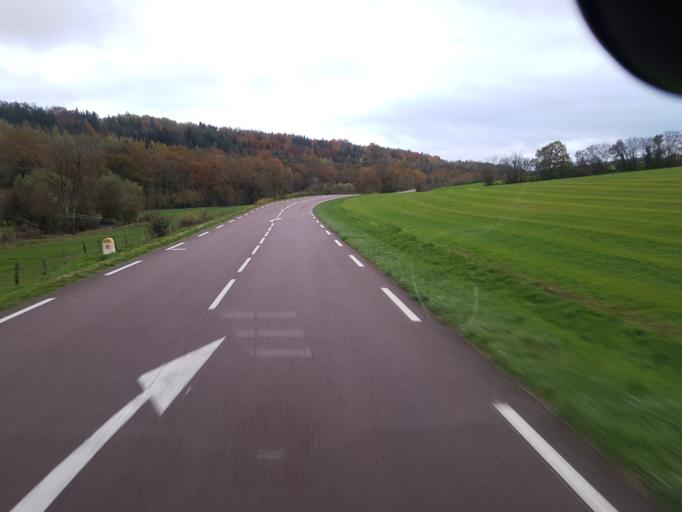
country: FR
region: Bourgogne
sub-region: Departement de la Cote-d'Or
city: Chatillon-sur-Seine
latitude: 47.6781
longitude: 4.6977
